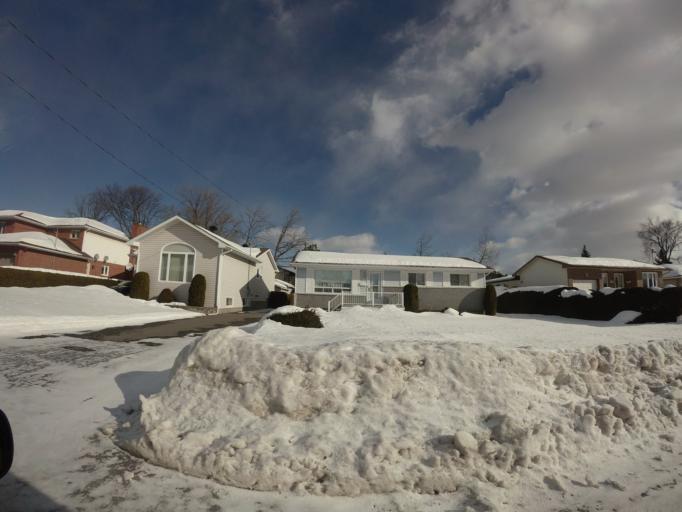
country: CA
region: Ontario
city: Ottawa
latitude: 45.4261
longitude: -75.6084
